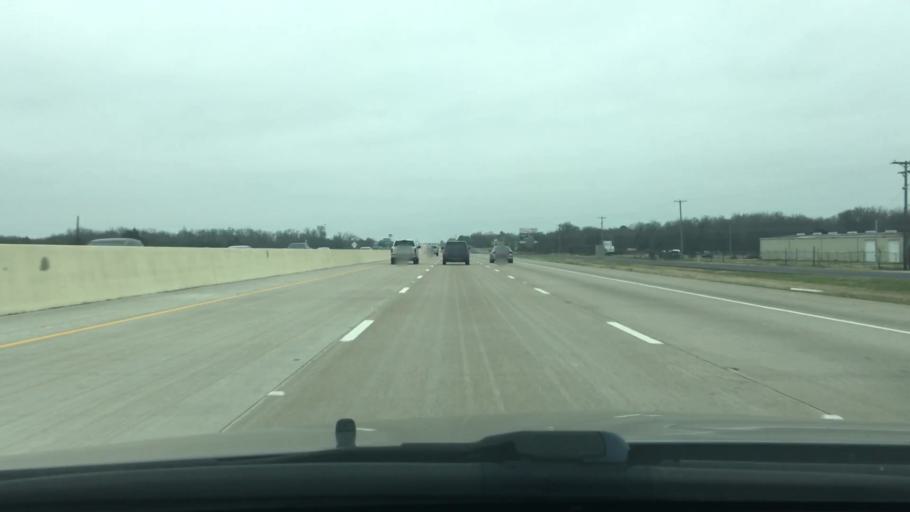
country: US
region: Texas
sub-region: Navarro County
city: Corsicana
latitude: 32.0233
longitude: -96.4401
